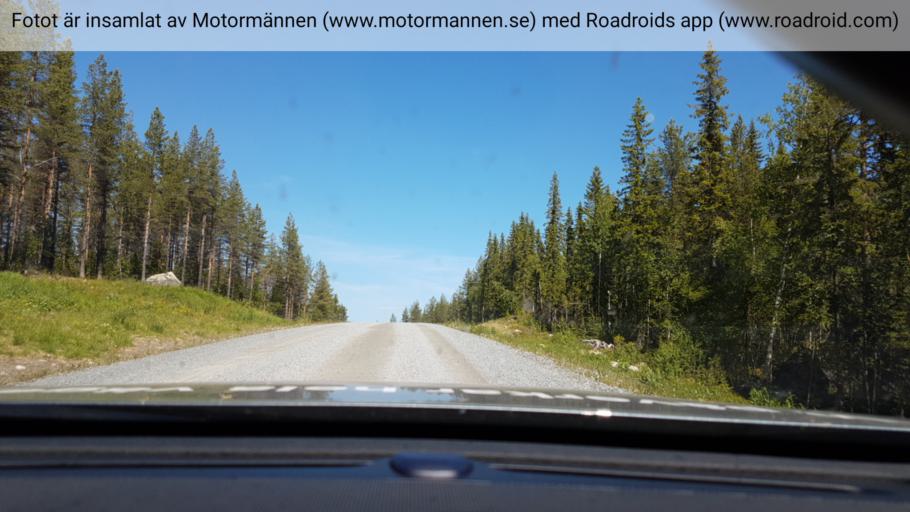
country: SE
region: Vaesterbotten
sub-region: Vilhelmina Kommun
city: Sjoberg
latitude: 64.6712
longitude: 15.7583
